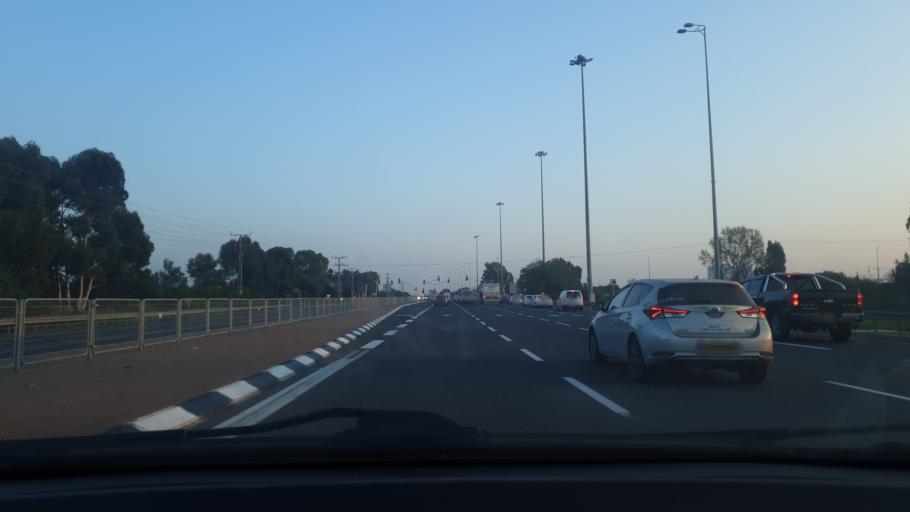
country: IL
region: Central District
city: Ramla
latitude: 31.9534
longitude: 34.8555
